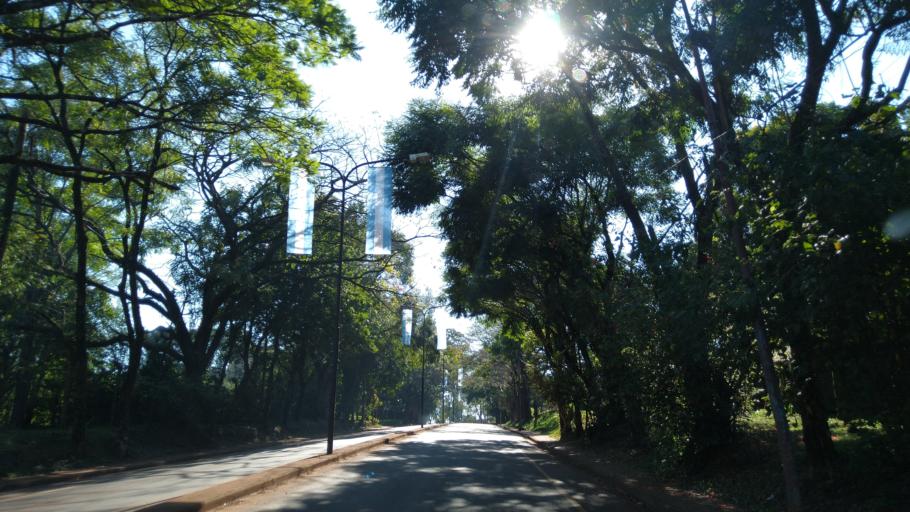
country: AR
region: Misiones
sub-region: Departamento de Montecarlo
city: Montecarlo
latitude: -26.5705
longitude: -54.7280
